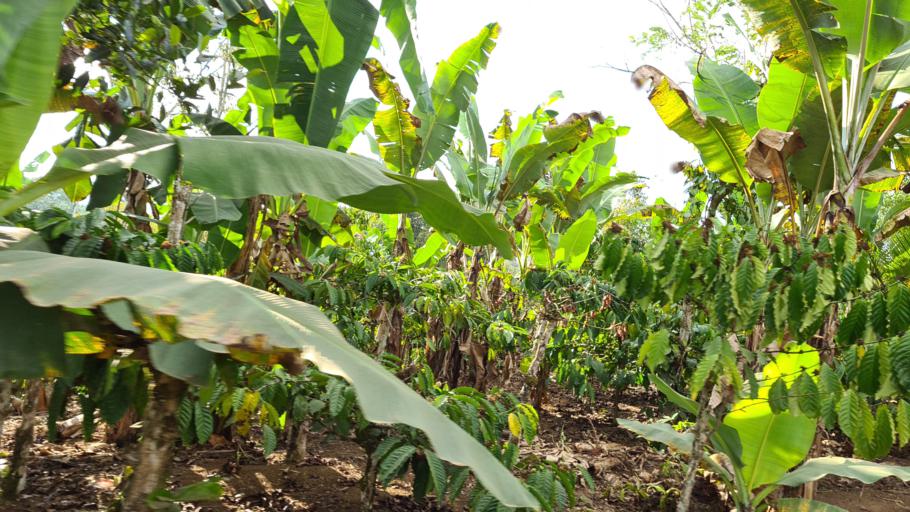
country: ID
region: Lampung
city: Kenali
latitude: -5.0823
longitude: 104.4067
